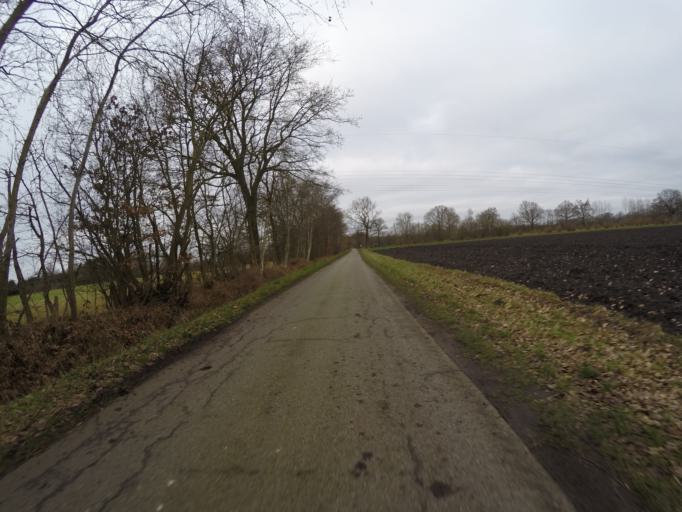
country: DE
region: Schleswig-Holstein
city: Hemdingen
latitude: 53.7703
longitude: 9.8434
